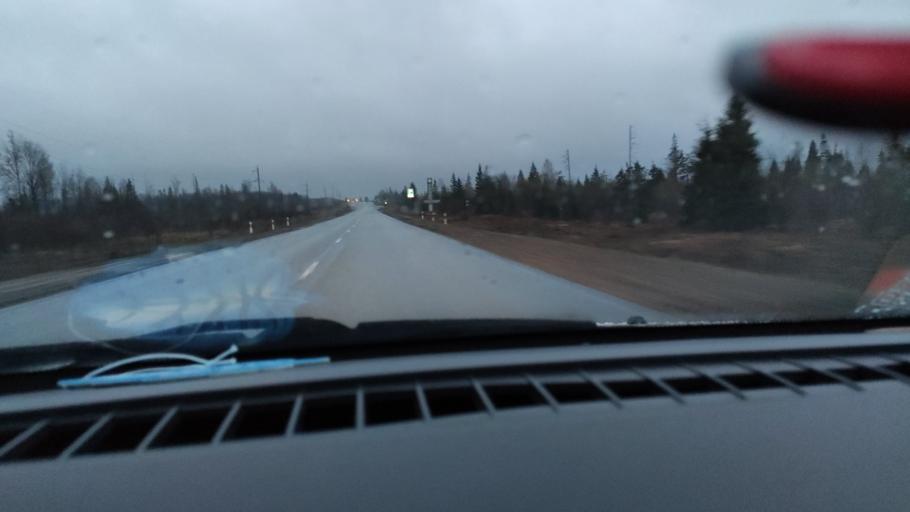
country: RU
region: Udmurtiya
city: Alnashi
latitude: 56.2640
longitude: 52.3699
